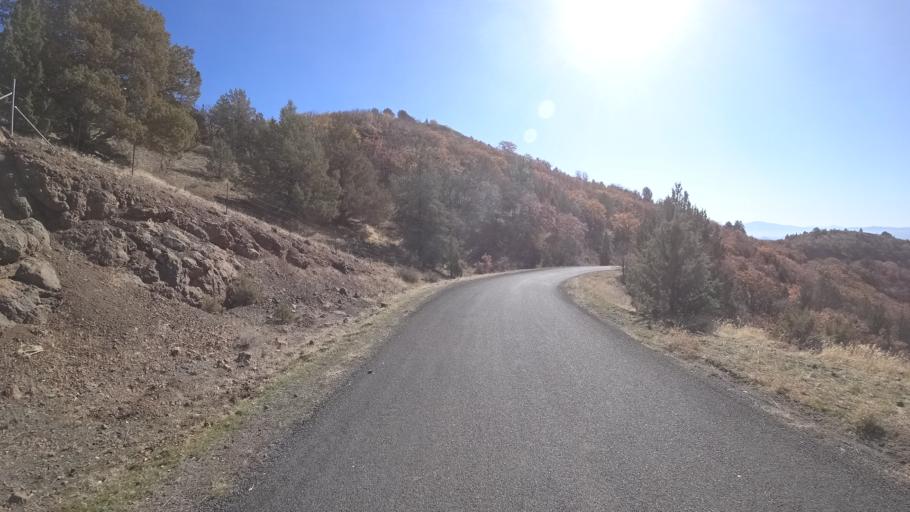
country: US
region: California
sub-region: Siskiyou County
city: Montague
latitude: 41.8302
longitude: -122.3324
